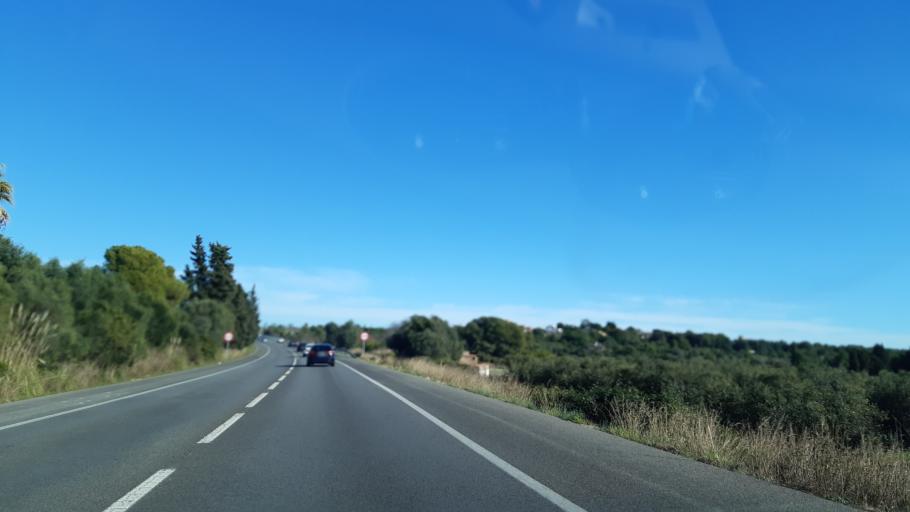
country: ES
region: Catalonia
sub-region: Provincia de Barcelona
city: Cubelles
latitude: 41.2128
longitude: 1.6930
